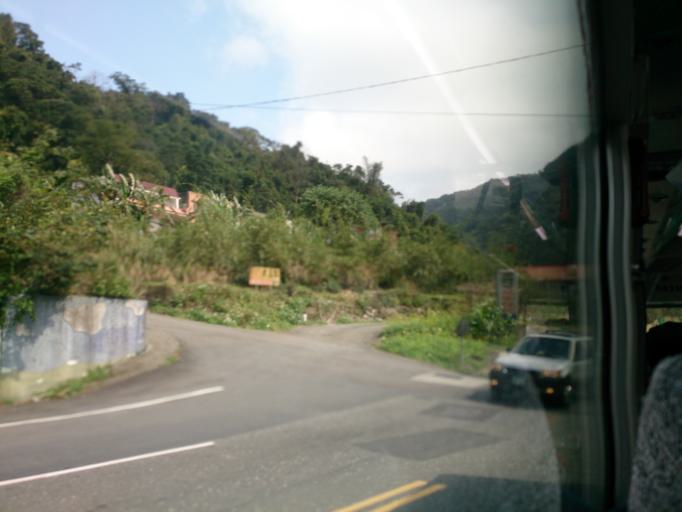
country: TW
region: Taipei
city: Taipei
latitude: 25.0090
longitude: 121.6495
